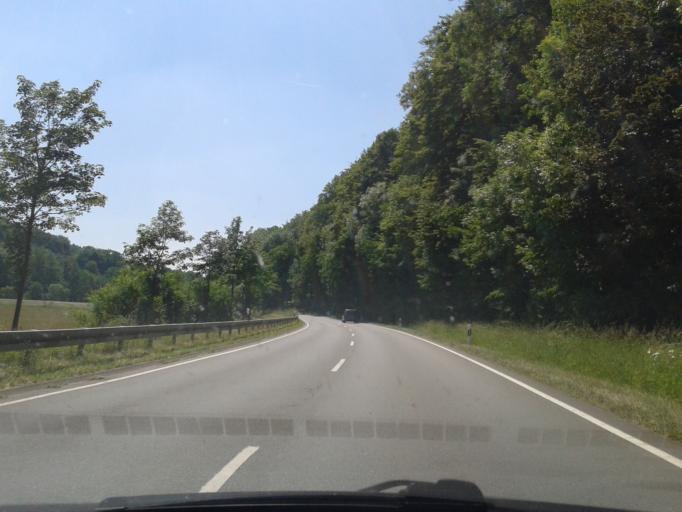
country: DE
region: North Rhine-Westphalia
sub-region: Regierungsbezirk Detmold
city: Blomberg
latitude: 51.9106
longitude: 9.1228
